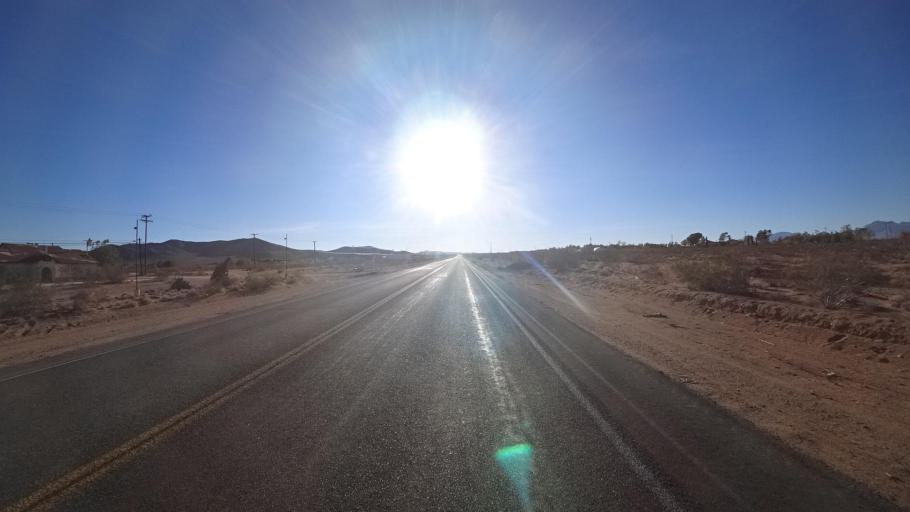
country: US
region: California
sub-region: Kern County
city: Ridgecrest
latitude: 35.5919
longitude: -117.6937
